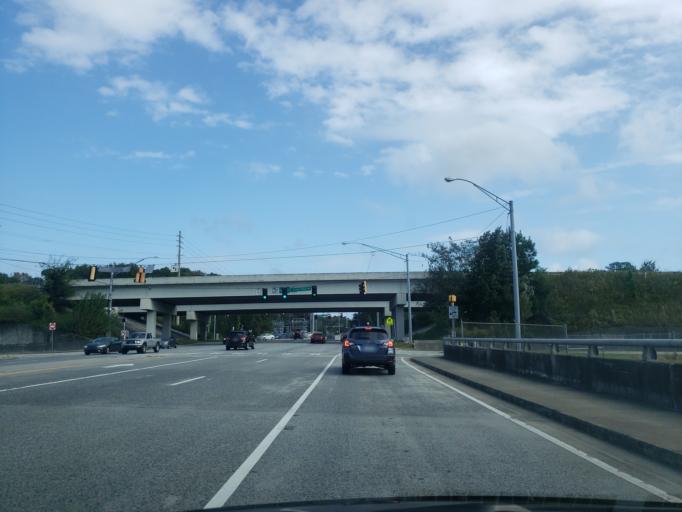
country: US
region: Georgia
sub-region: Chatham County
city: Thunderbolt
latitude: 32.0228
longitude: -81.0894
